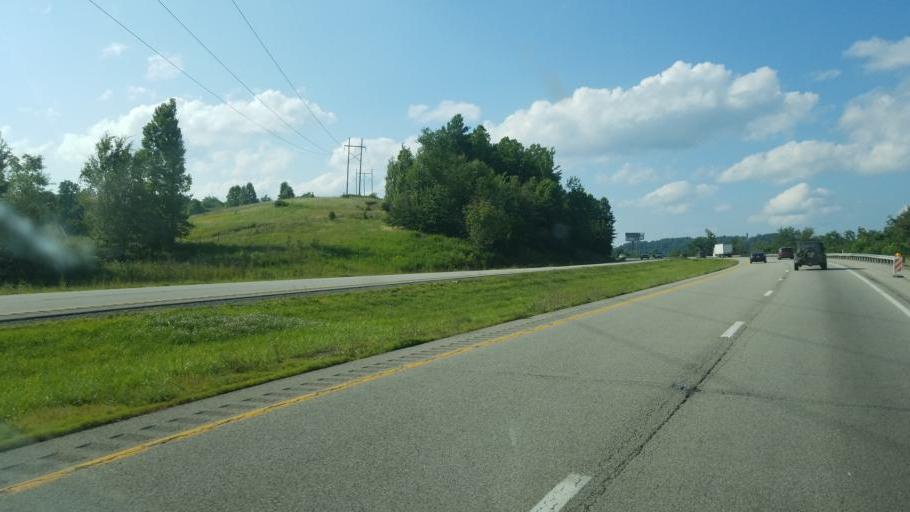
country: US
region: West Virginia
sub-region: Monongalia County
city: Star City
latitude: 39.6855
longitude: -80.0404
